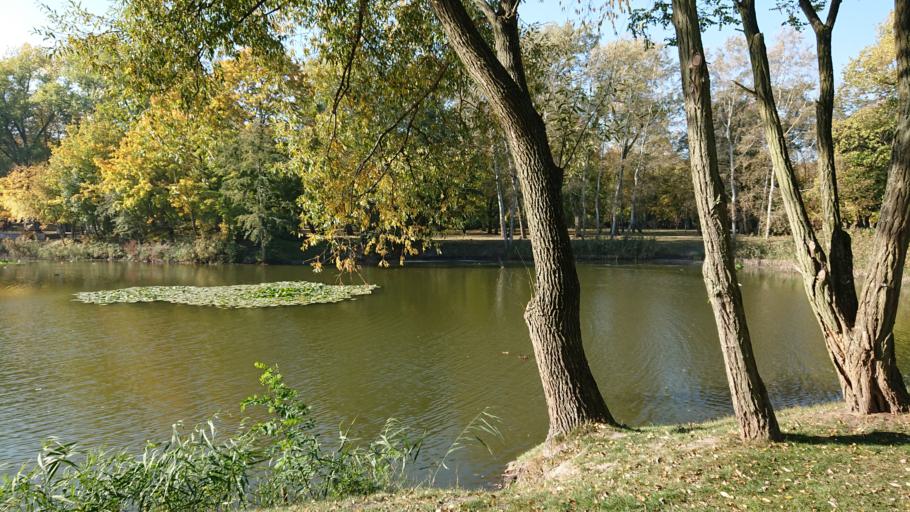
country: PL
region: Kujawsko-Pomorskie
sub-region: Powiat inowroclawski
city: Inowroclaw
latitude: 52.7925
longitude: 18.2419
